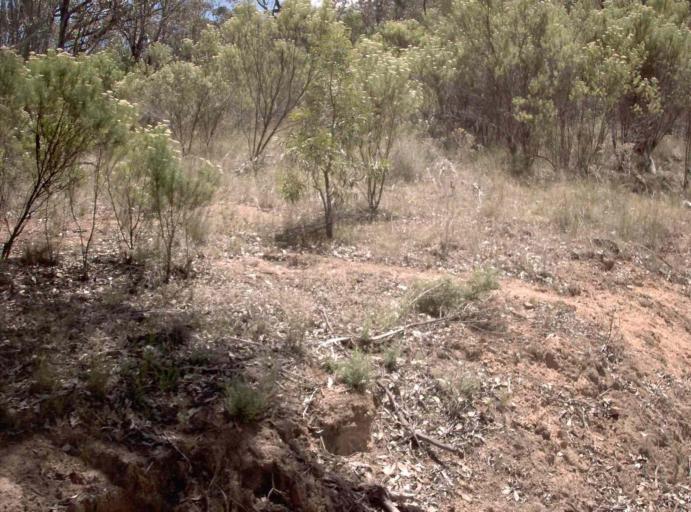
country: AU
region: New South Wales
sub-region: Snowy River
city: Jindabyne
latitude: -36.9392
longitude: 148.3396
